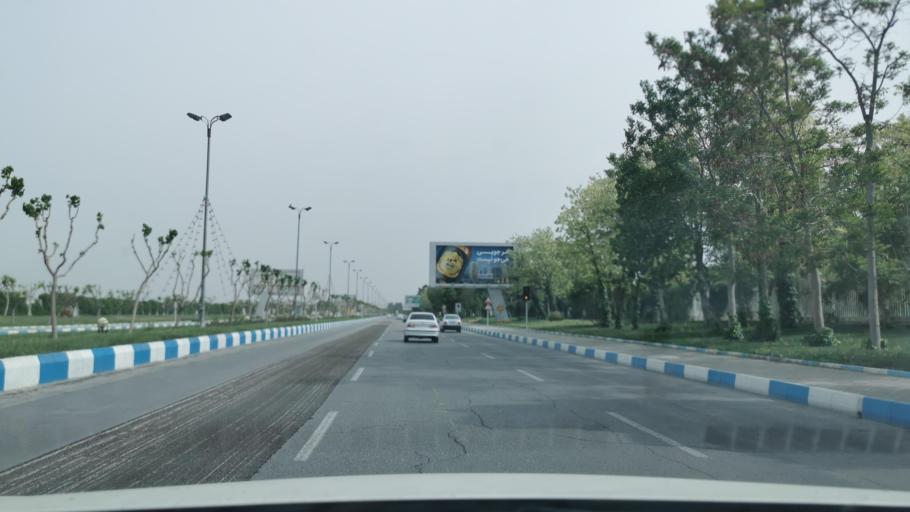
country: IR
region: Razavi Khorasan
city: Mashhad
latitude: 36.2392
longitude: 59.6274
